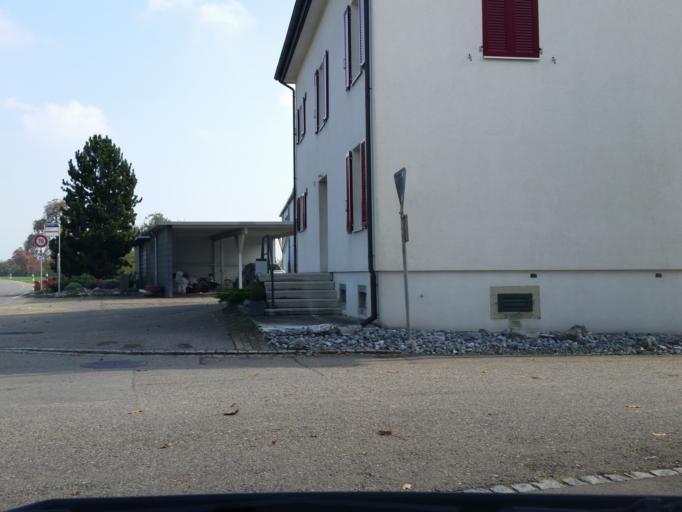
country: CH
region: Thurgau
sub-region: Arbon District
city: Uttwil
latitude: 47.5562
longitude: 9.3349
